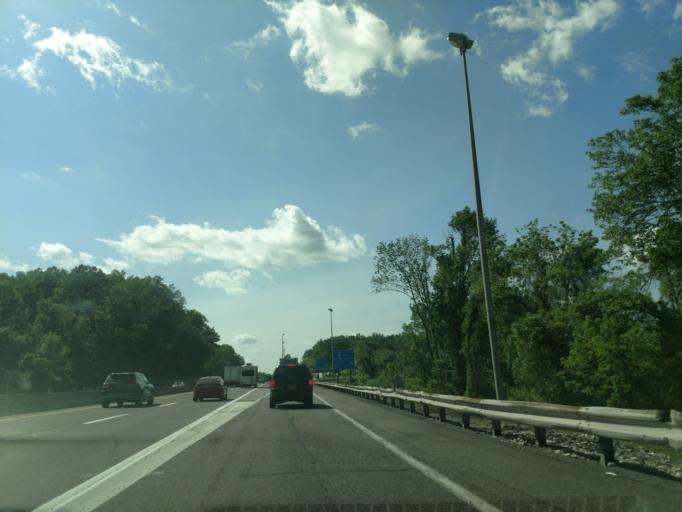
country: US
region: Pennsylvania
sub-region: Chester County
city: Elverson
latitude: 40.1204
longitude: -75.7742
